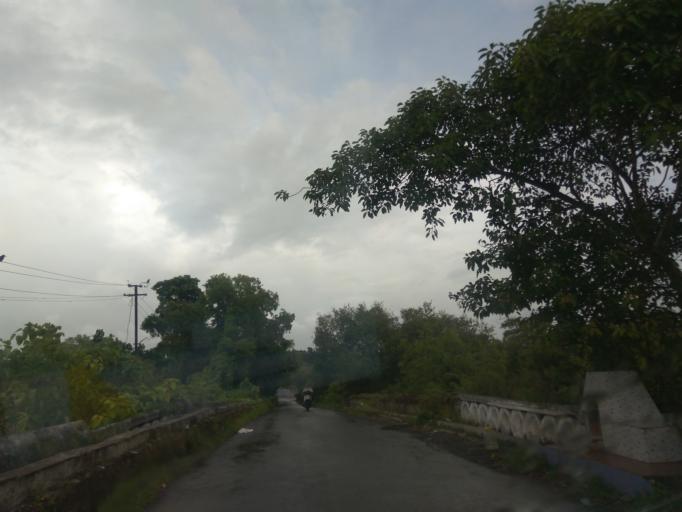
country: IN
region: Goa
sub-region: North Goa
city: Goa Velha
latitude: 15.4428
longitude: 73.8668
